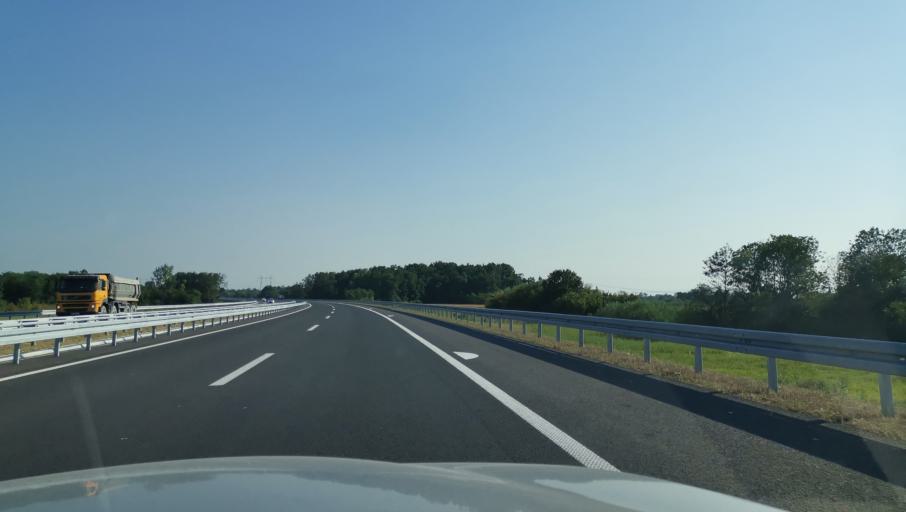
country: RS
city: Zvecka
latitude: 44.6183
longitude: 20.1932
